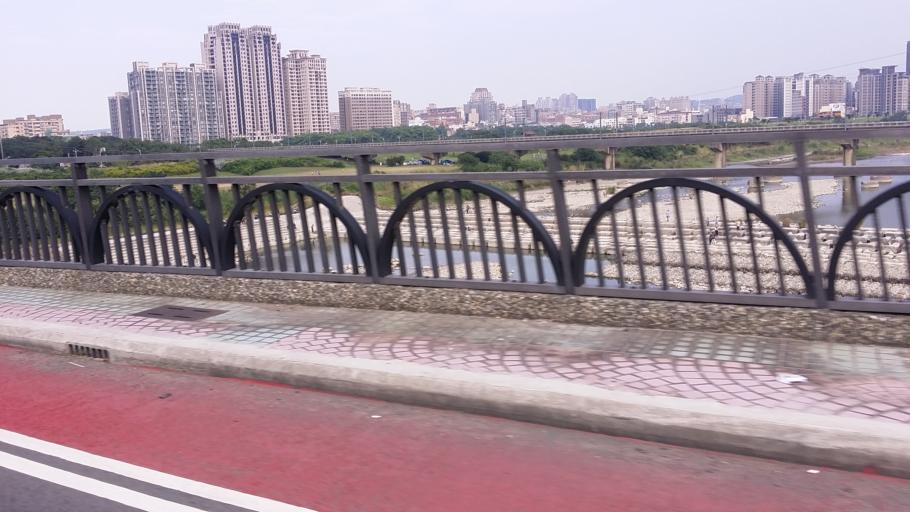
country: TW
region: Taiwan
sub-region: Hsinchu
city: Zhubei
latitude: 24.8229
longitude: 120.9968
